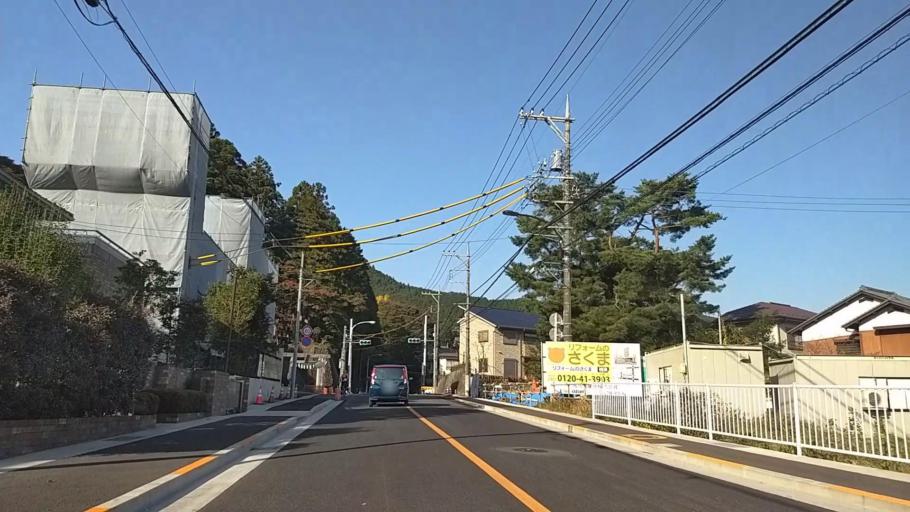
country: JP
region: Tokyo
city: Ome
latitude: 35.7847
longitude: 139.2362
